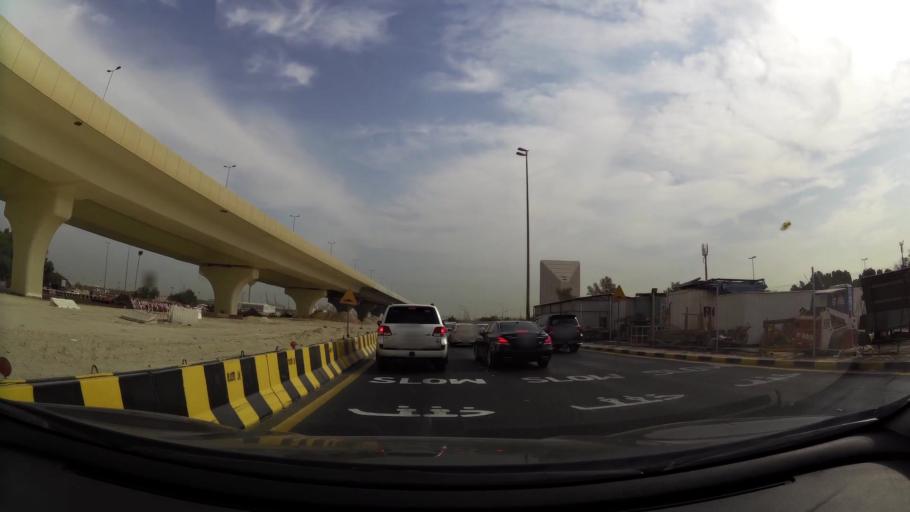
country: KW
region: Al Asimah
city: Ar Rabiyah
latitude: 29.3313
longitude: 47.9078
